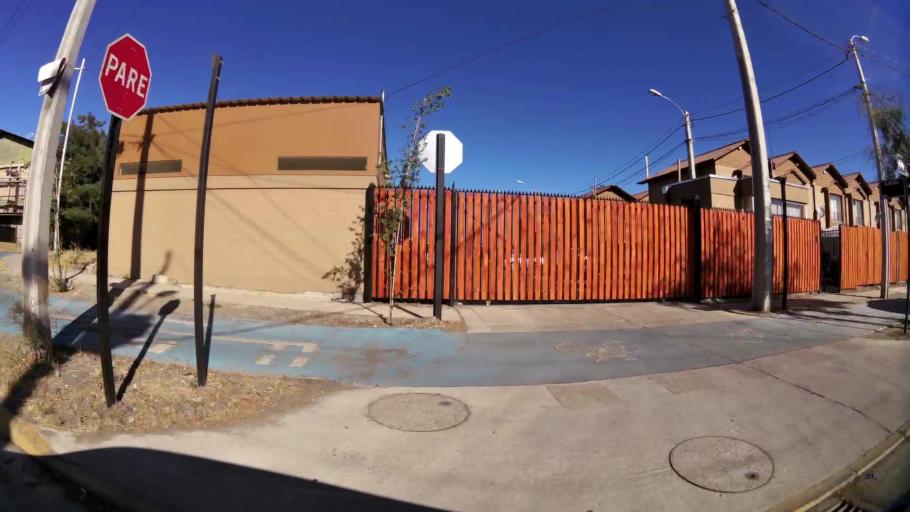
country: CL
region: O'Higgins
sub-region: Provincia de Cachapoal
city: Rancagua
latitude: -34.1778
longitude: -70.7548
